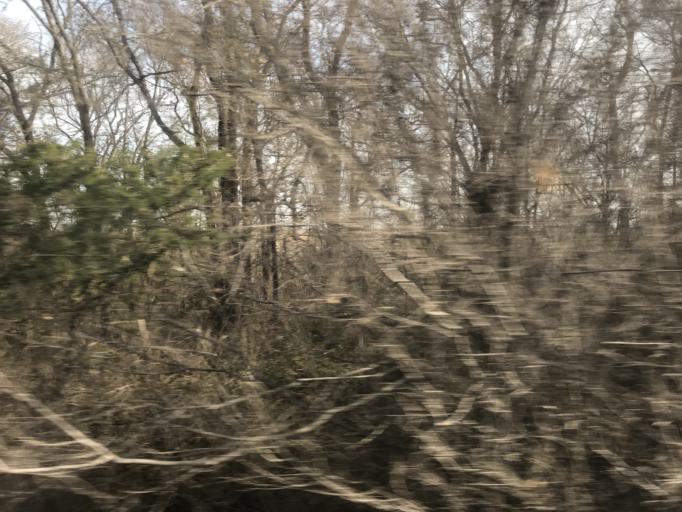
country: AR
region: Cordoba
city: Laguna Larga
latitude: -31.7403
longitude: -63.8350
